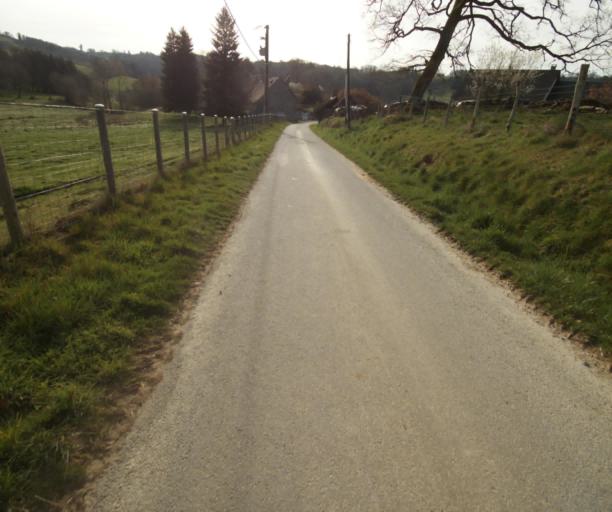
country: FR
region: Limousin
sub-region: Departement de la Correze
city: Chamboulive
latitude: 45.4464
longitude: 1.7522
